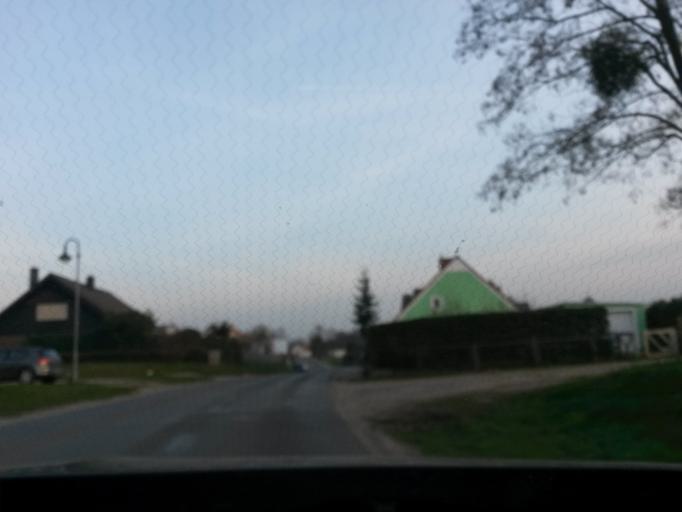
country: DE
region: Brandenburg
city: Protzel
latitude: 52.5938
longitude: 13.9481
